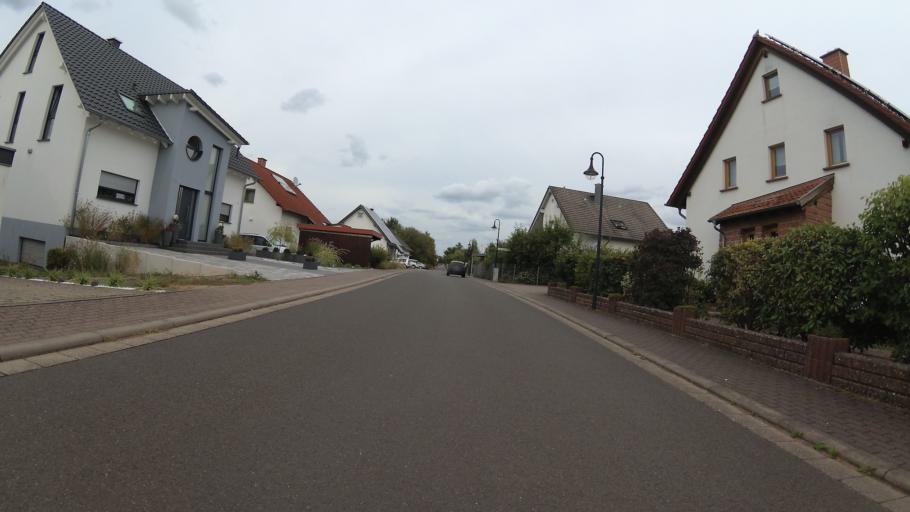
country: DE
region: Saarland
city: Bexbach
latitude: 49.3120
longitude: 7.2706
